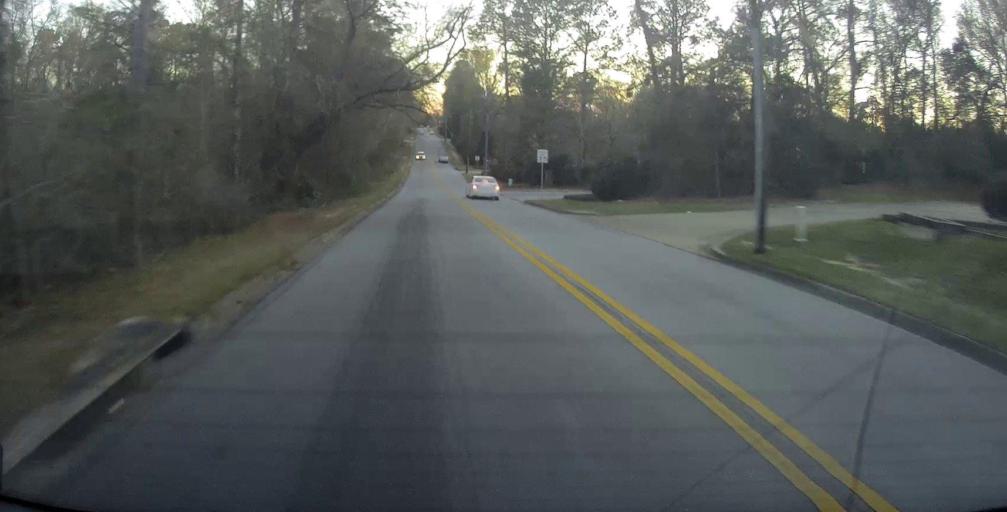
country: US
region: Alabama
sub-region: Russell County
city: Phenix City
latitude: 32.4908
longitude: -85.0190
